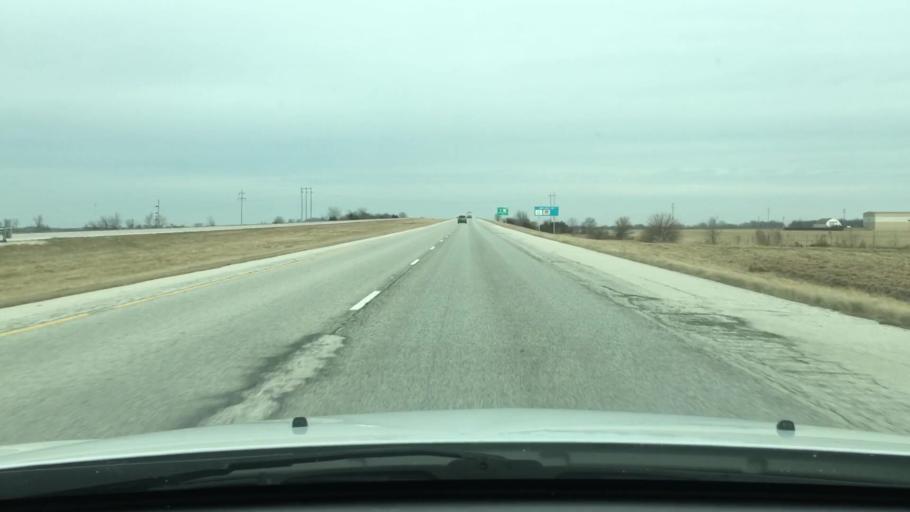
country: US
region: Illinois
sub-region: Morgan County
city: South Jacksonville
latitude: 39.7050
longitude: -90.1858
